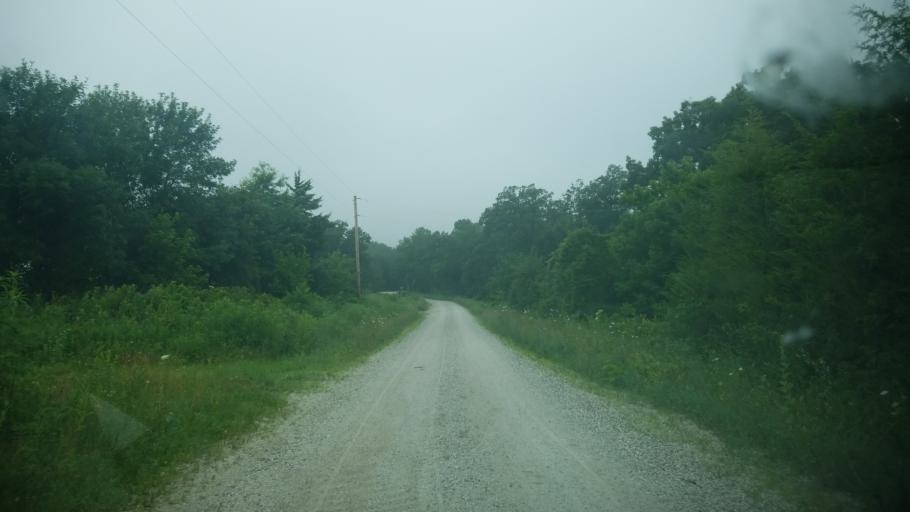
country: US
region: Missouri
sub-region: Audrain County
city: Vandalia
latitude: 39.2726
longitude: -91.3435
